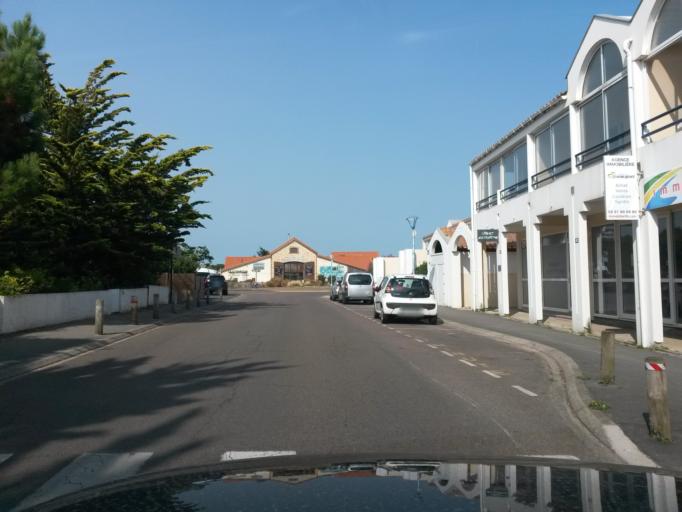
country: FR
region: Pays de la Loire
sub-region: Departement de la Vendee
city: Bretignolles-sur-Mer
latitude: 46.6170
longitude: -1.8639
